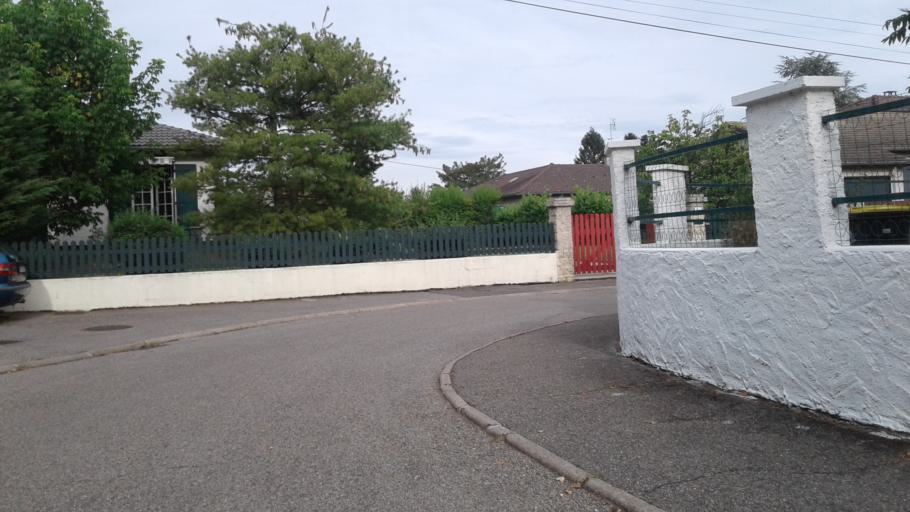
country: FR
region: Rhone-Alpes
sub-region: Departement de l'Ain
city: Beynost
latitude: 45.8339
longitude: 5.0025
